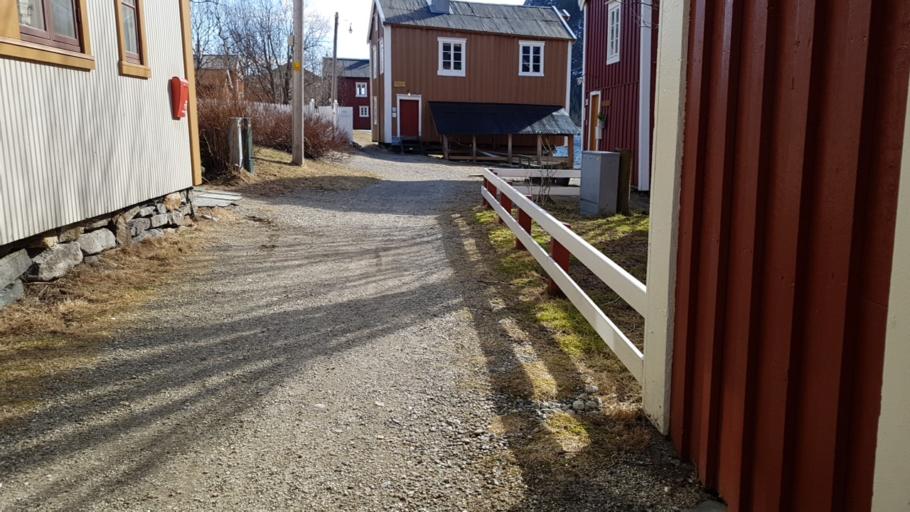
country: NO
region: Nordland
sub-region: Vefsn
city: Mosjoen
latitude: 65.8368
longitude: 13.1880
